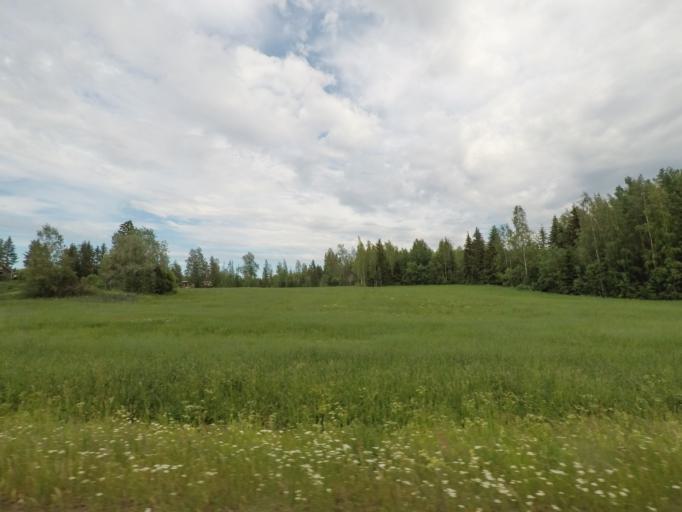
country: FI
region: Paijanne Tavastia
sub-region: Lahti
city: Hollola
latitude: 60.8193
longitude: 25.4850
